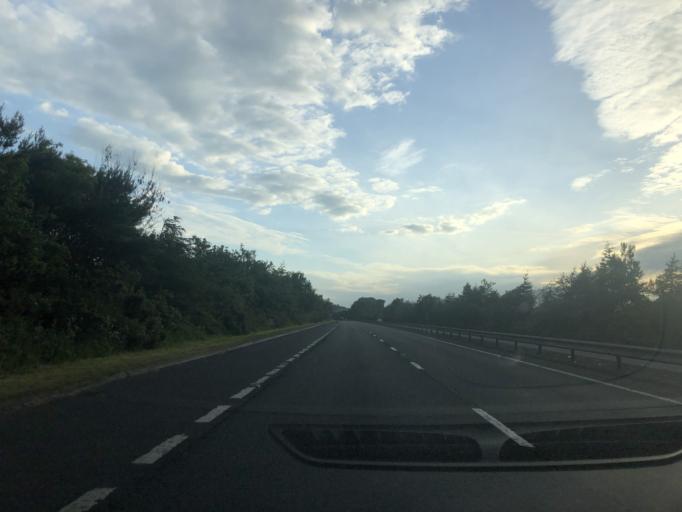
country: GB
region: Scotland
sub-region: Fife
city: Kirkcaldy
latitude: 56.1427
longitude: -3.1853
